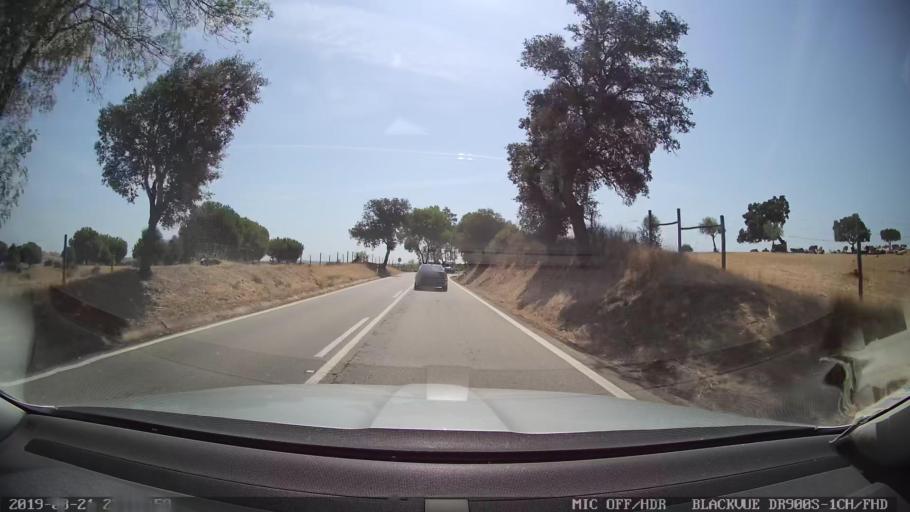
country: PT
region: Castelo Branco
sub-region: Idanha-A-Nova
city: Idanha-a-Nova
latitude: 39.8619
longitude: -7.3176
